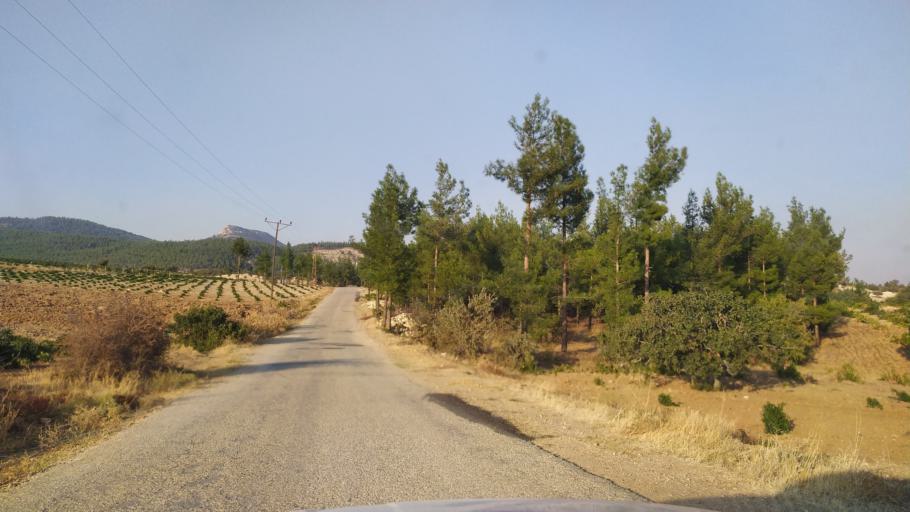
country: TR
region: Mersin
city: Mut
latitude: 36.6875
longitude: 33.1966
